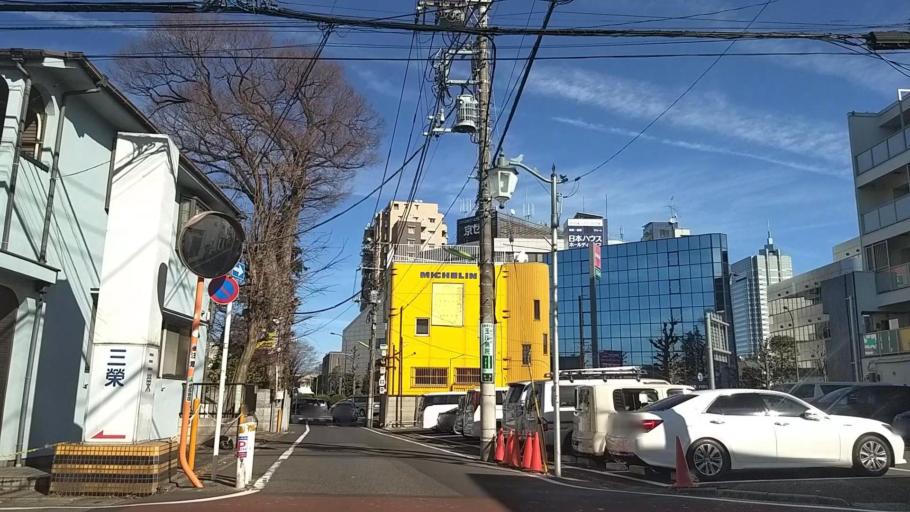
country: JP
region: Tokyo
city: Chofugaoka
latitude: 35.6233
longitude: 139.6272
